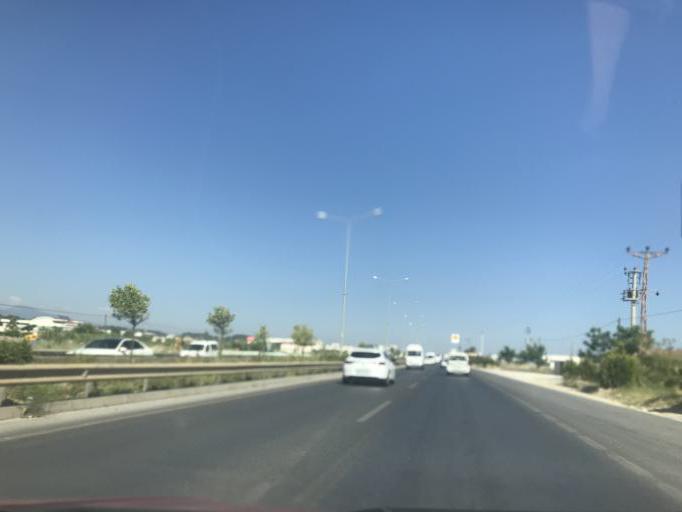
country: TR
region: Antalya
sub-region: Manavgat
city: Side
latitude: 36.8129
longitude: 31.3715
